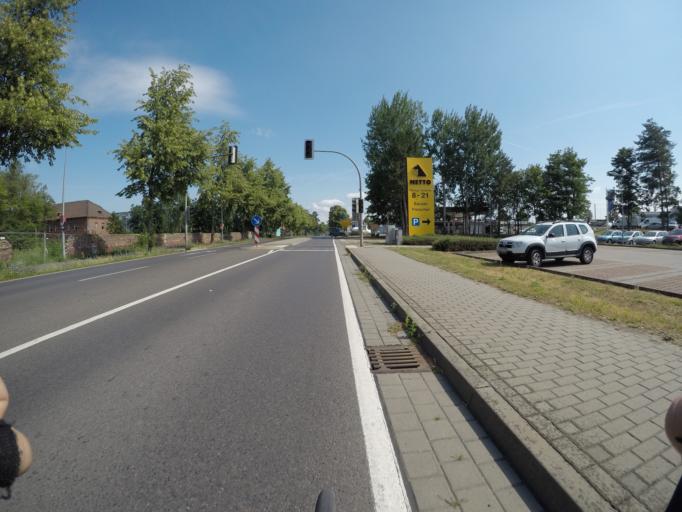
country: DE
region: Brandenburg
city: Bernau bei Berlin
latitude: 52.6676
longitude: 13.5815
